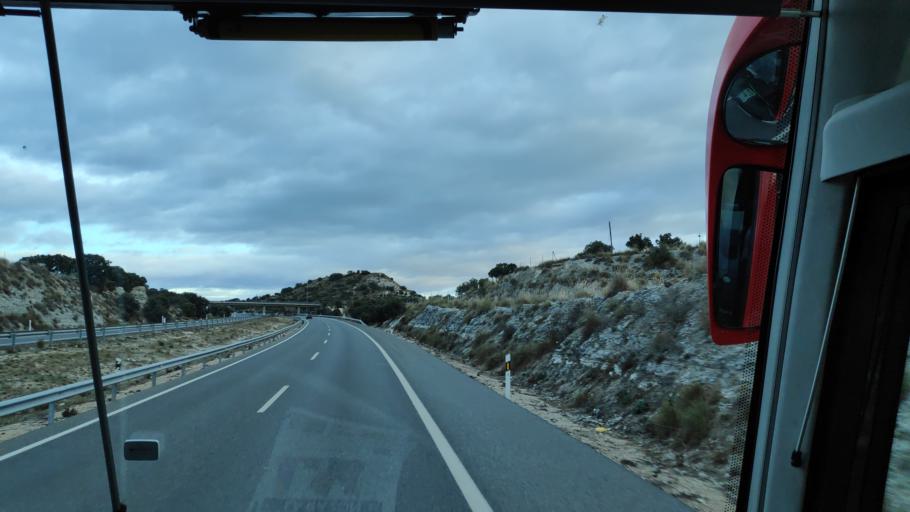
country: ES
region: Madrid
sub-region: Provincia de Madrid
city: Fuentiduena de Tajo
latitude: 40.1429
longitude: -3.2117
